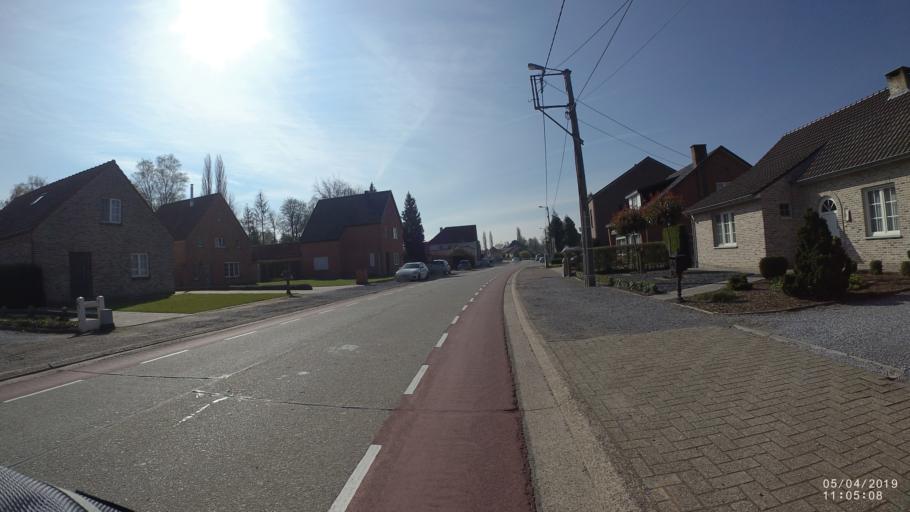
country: BE
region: Flanders
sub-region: Provincie Limburg
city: Lummen
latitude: 50.9560
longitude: 5.1940
